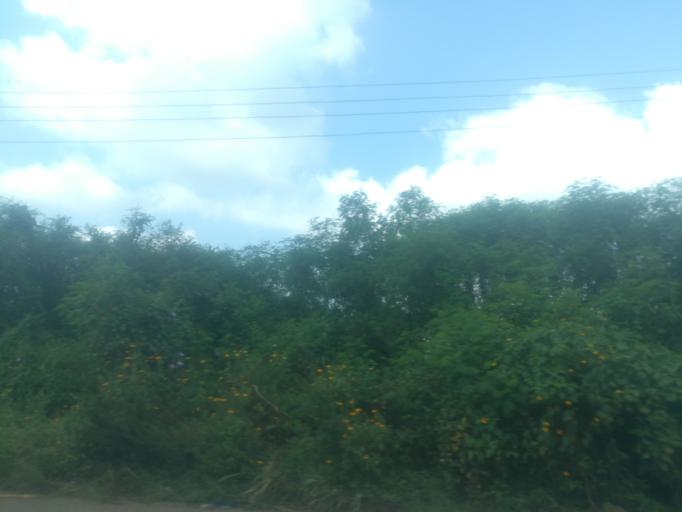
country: NG
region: Oyo
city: Moniya
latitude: 7.5686
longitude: 3.9143
